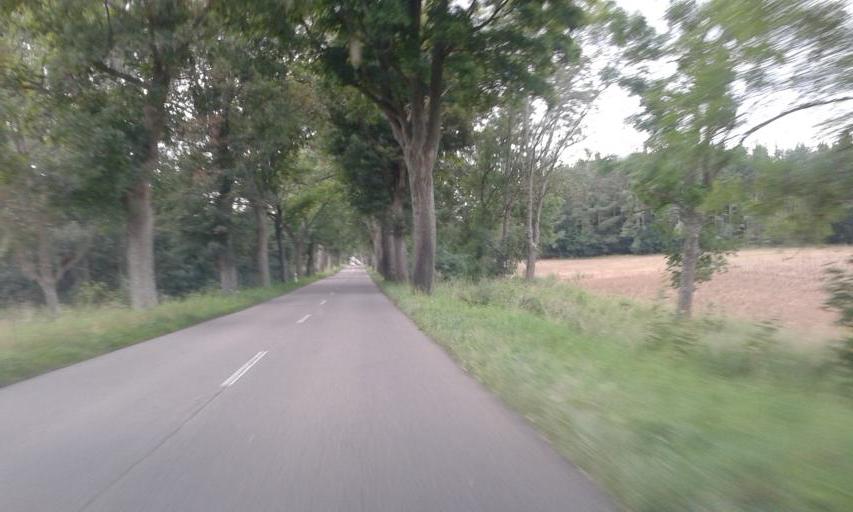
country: PL
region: West Pomeranian Voivodeship
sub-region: Powiat szczecinecki
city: Barwice
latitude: 53.7520
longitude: 16.3148
